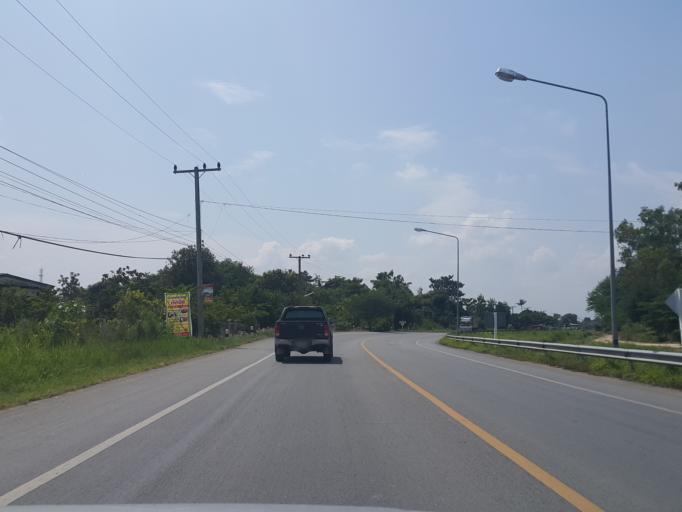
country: TH
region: Chiang Mai
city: San Pa Tong
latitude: 18.6588
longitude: 98.8673
